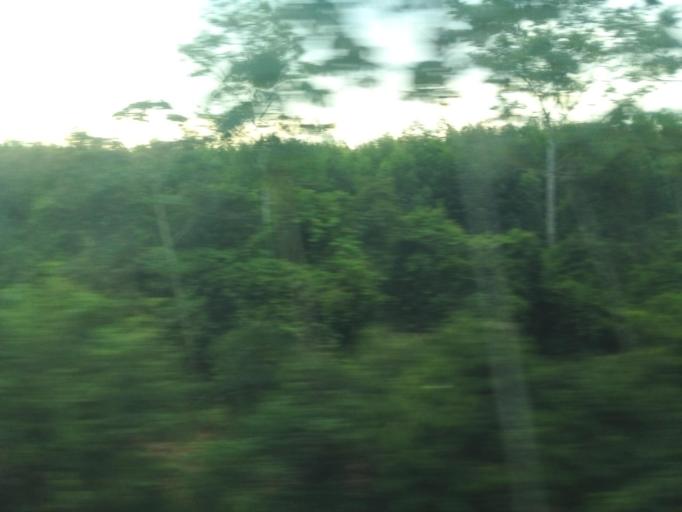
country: BR
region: Maranhao
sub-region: Imperatriz
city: Imperatriz
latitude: -4.7296
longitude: -47.3078
